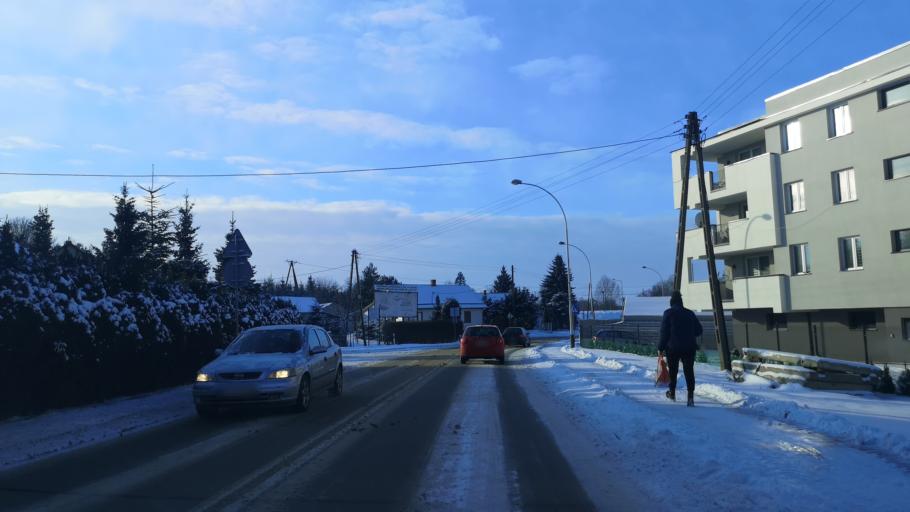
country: PL
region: Subcarpathian Voivodeship
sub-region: Powiat przeworski
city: Przeworsk
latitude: 50.0734
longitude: 22.4928
